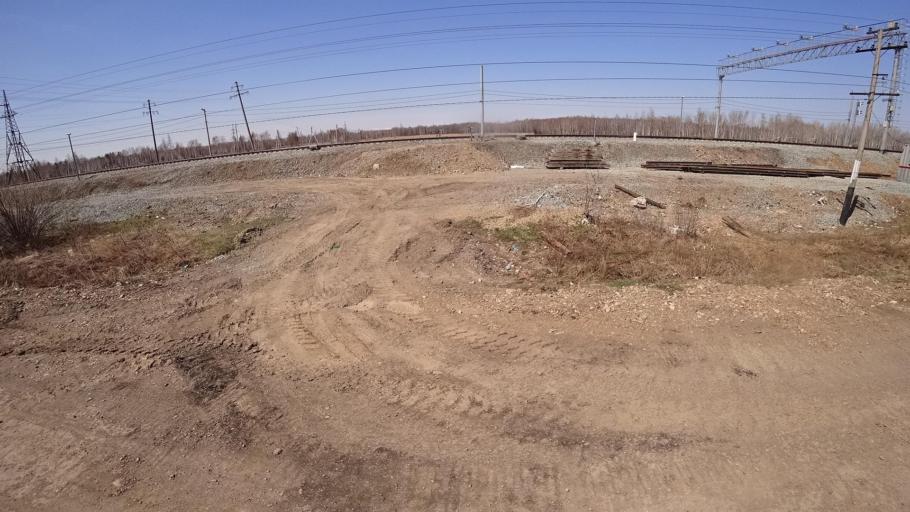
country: RU
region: Khabarovsk Krai
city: Khurba
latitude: 50.4036
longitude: 136.8696
